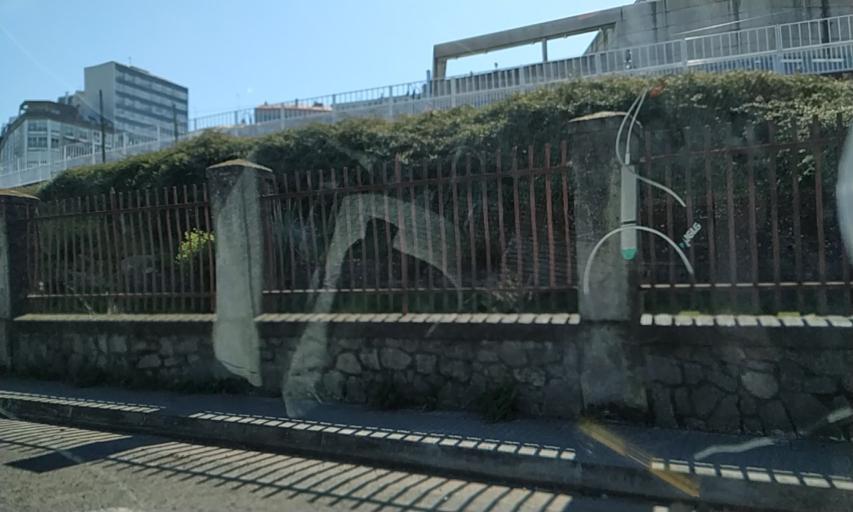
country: ES
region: Galicia
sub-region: Provincia da Coruna
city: A Coruna
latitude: 43.3549
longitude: -8.3892
